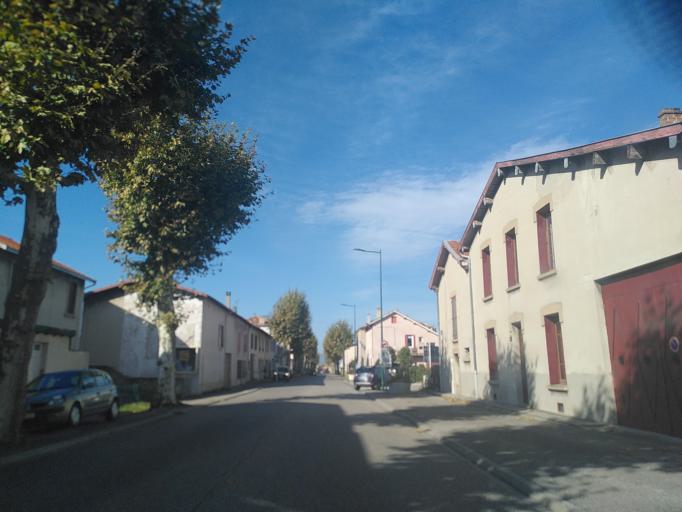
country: FR
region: Rhone-Alpes
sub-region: Departement de l'Isere
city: Chanas
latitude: 45.2860
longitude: 4.8171
